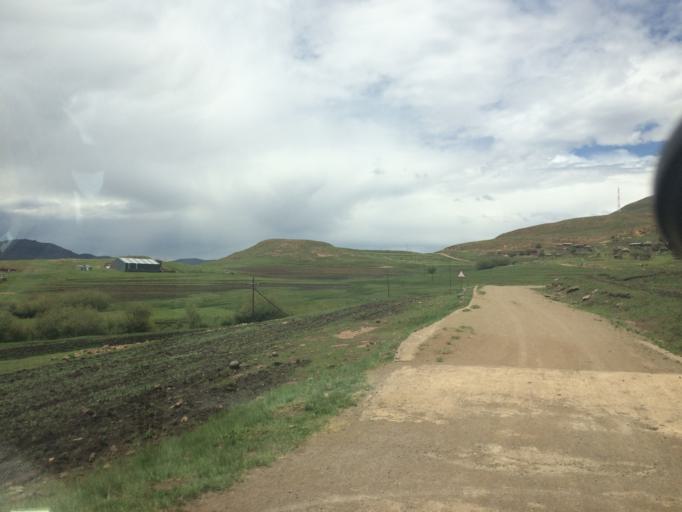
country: LS
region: Maseru
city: Nako
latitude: -29.8622
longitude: 28.0382
